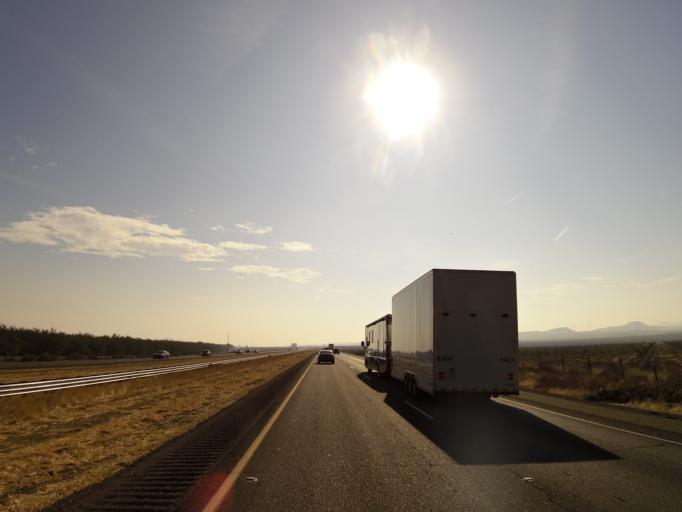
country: US
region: California
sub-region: Fresno County
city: Coalinga
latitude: 36.3627
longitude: -120.3290
